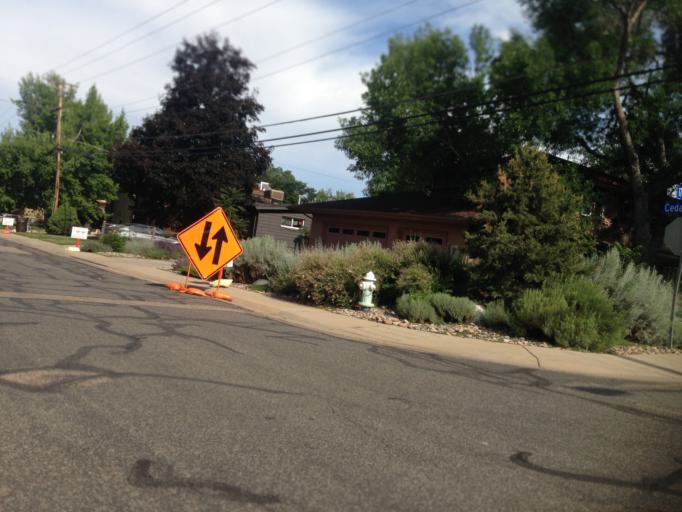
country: US
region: Colorado
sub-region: Boulder County
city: Boulder
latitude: 40.0280
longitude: -105.2749
